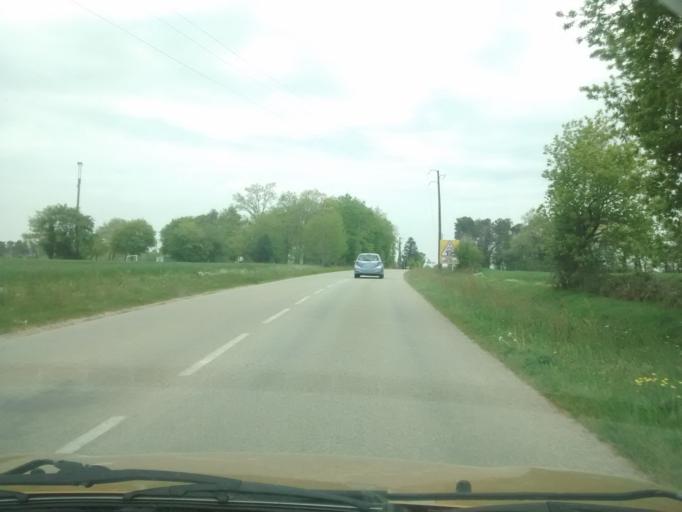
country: FR
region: Brittany
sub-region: Departement du Morbihan
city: Questembert
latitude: 47.6544
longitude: -2.4822
